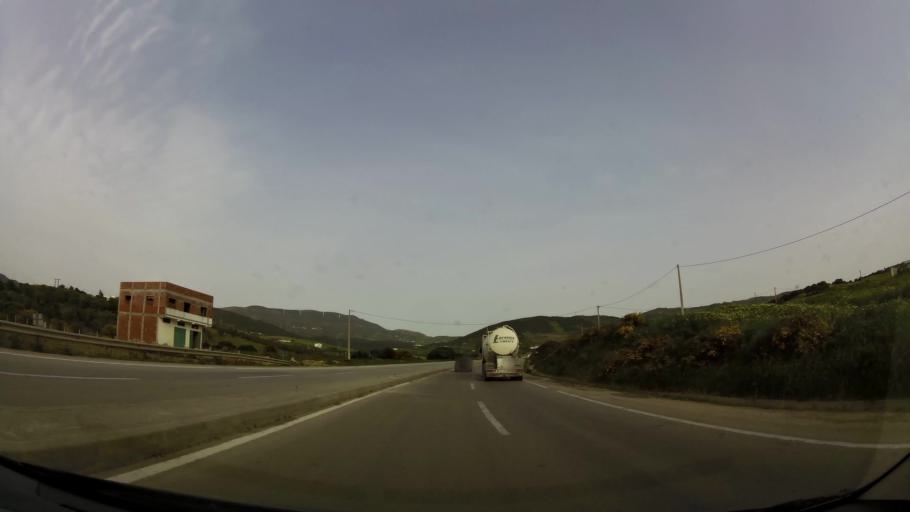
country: MA
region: Tanger-Tetouan
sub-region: Tanger-Assilah
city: Dar Chaoui
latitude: 35.5681
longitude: -5.6114
